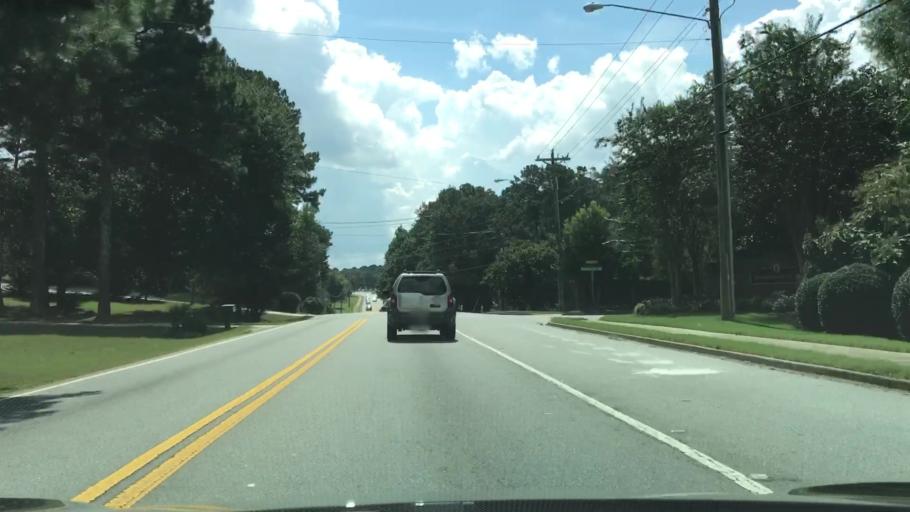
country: US
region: Georgia
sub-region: Gwinnett County
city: Snellville
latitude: 33.8771
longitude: -84.0537
